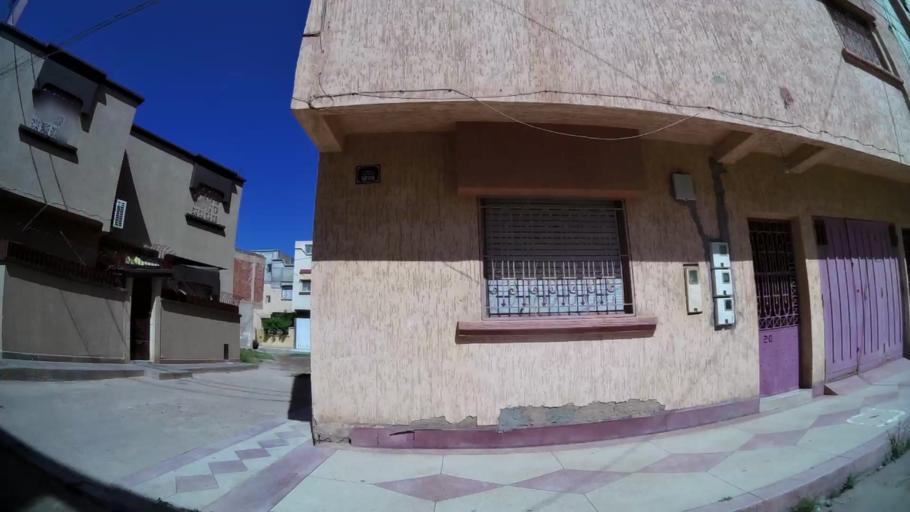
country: MA
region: Oriental
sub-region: Oujda-Angad
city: Oujda
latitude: 34.6758
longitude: -1.9335
